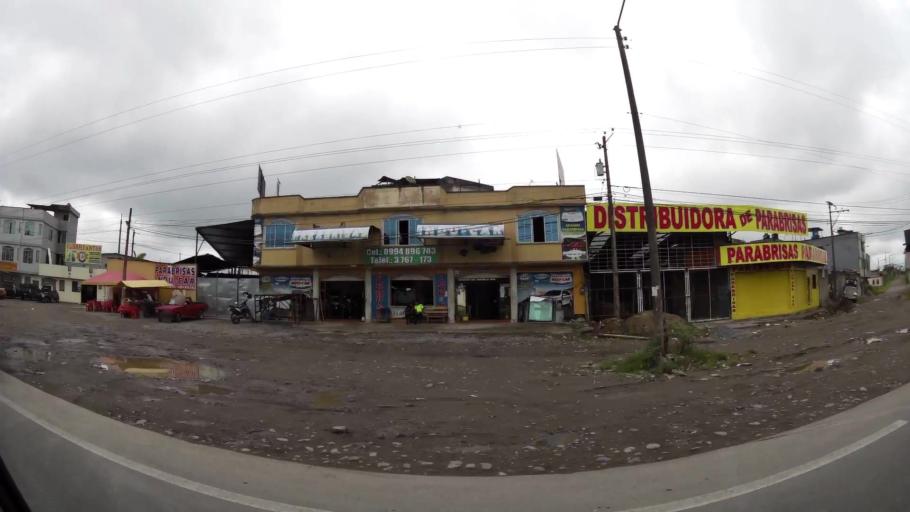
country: EC
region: Santo Domingo de los Tsachilas
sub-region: Canton Santo Domingo de los Colorados
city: Santo Domingo de los Colorados
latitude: -0.2451
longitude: -79.1987
